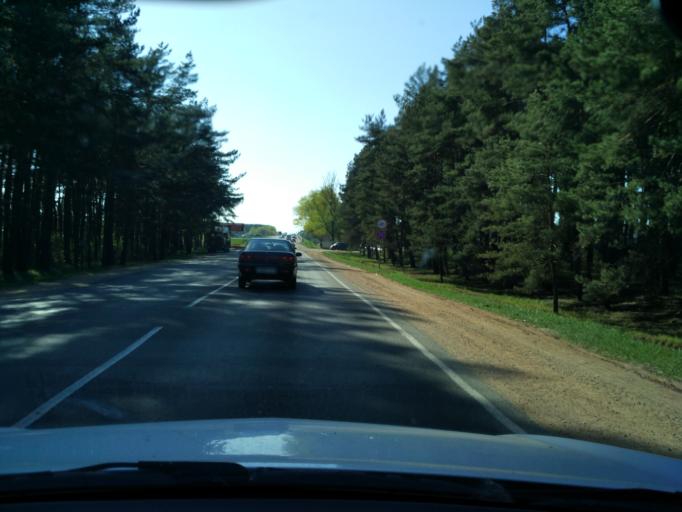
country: BY
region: Minsk
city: Borovlyany
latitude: 53.9661
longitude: 27.6529
